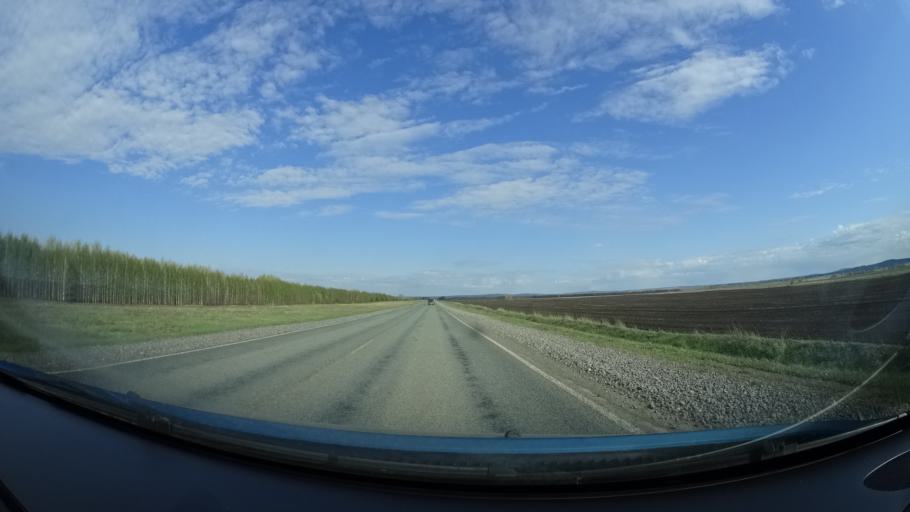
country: RU
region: Bashkortostan
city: Blagoveshchensk
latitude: 55.2009
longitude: 55.8261
